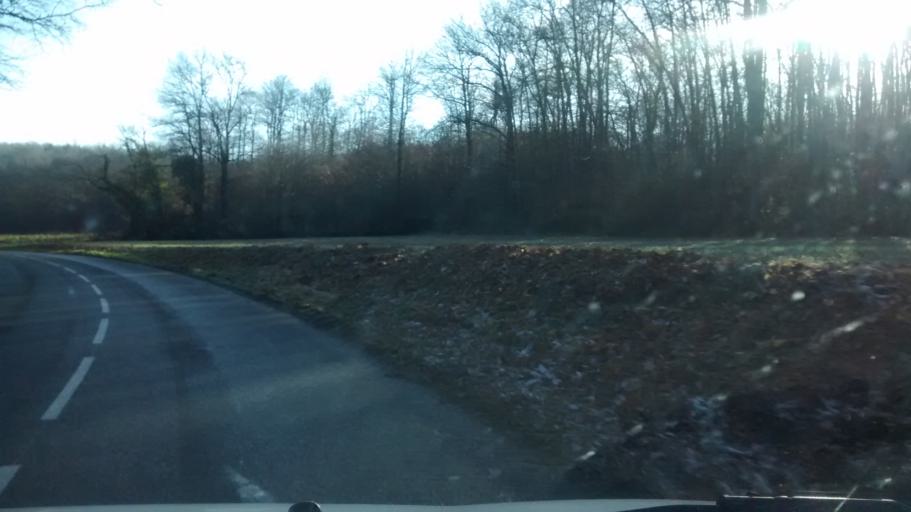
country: FR
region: Centre
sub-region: Departement d'Indre-et-Loire
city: Reugny
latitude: 47.4828
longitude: 0.8723
